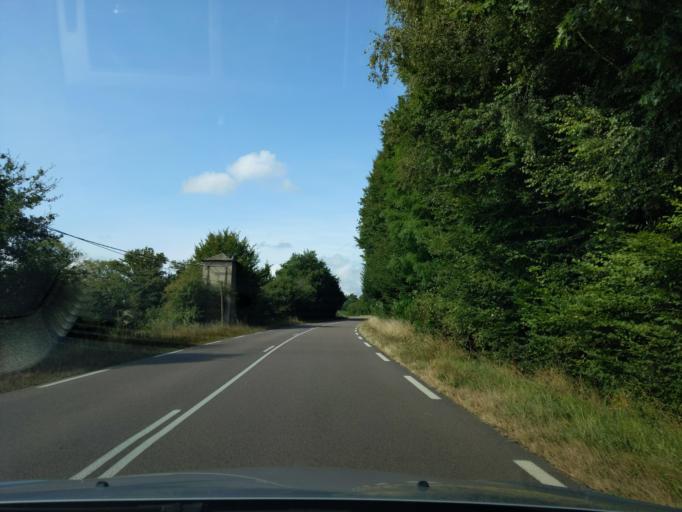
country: FR
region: Bourgogne
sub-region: Departement de Saone-et-Loire
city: Etang-sur-Arroux
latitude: 46.8721
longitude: 4.1309
